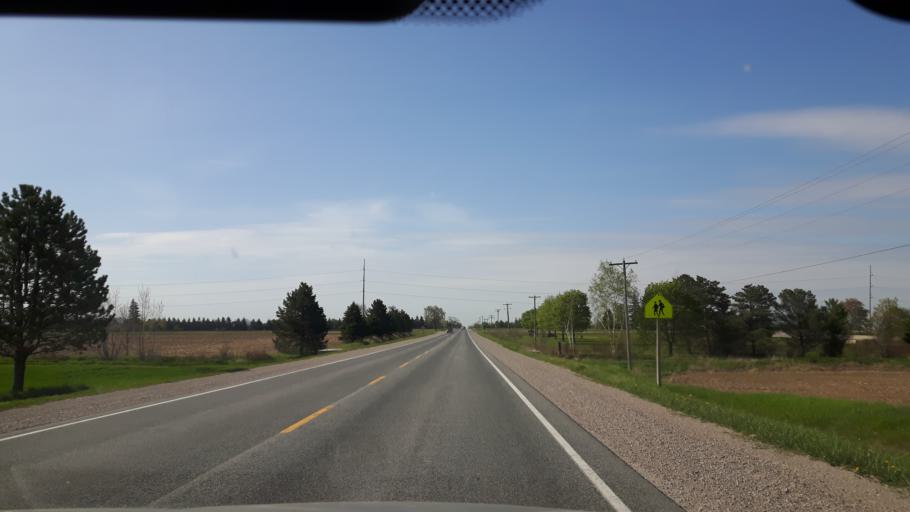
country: CA
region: Ontario
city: Bluewater
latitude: 43.5100
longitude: -81.5141
